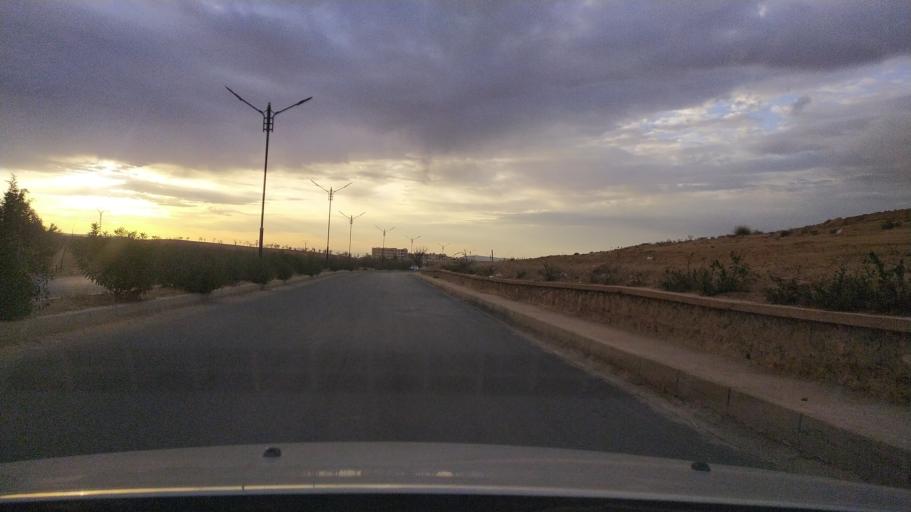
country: DZ
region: Tiaret
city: Frenda
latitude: 35.0515
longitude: 1.0694
